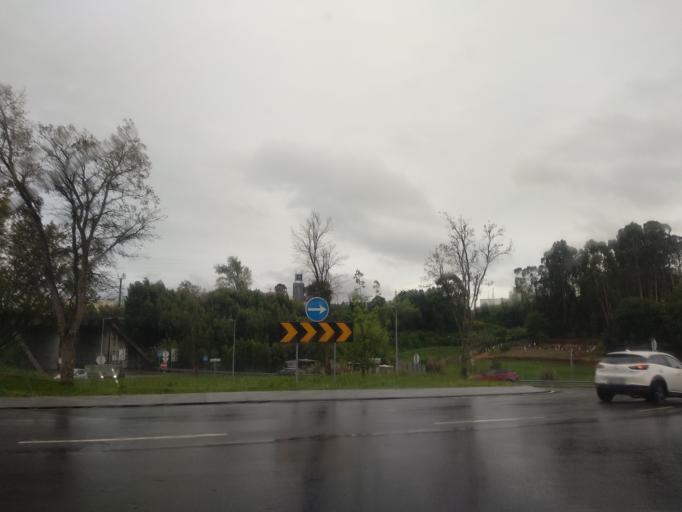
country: PT
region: Porto
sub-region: Gondomar
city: Rio Tinto
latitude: 41.1786
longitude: -8.5643
